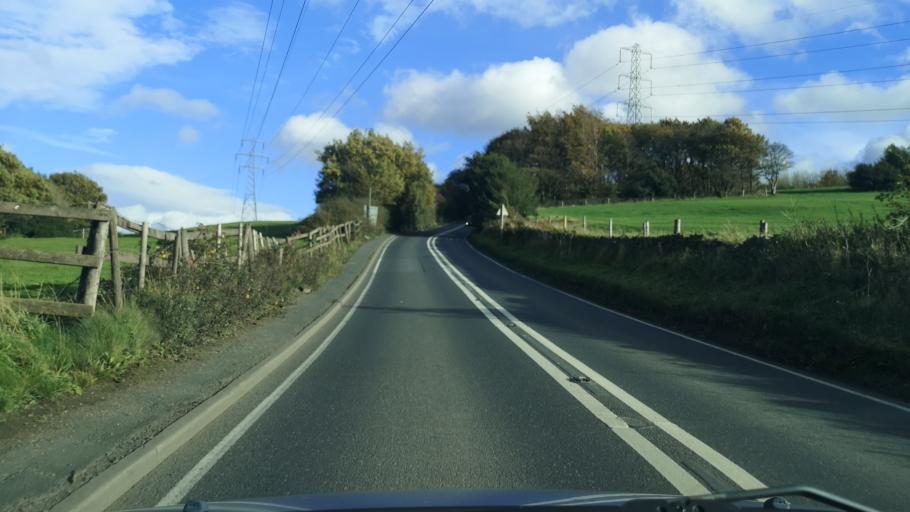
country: GB
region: England
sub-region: Kirklees
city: Mirfield
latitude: 53.6509
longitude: -1.6883
